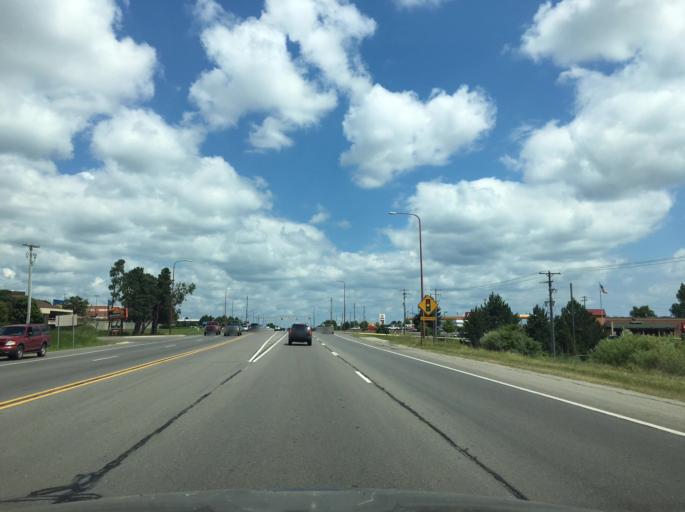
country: US
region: Michigan
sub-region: Grand Traverse County
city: Traverse City
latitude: 44.7204
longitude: -85.6460
